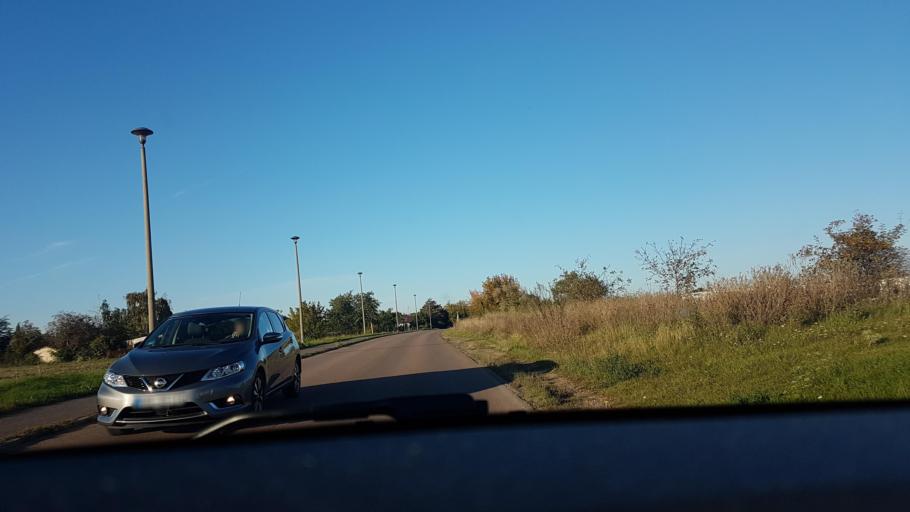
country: DE
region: Saxony-Anhalt
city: Bernburg
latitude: 51.7775
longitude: 11.7338
